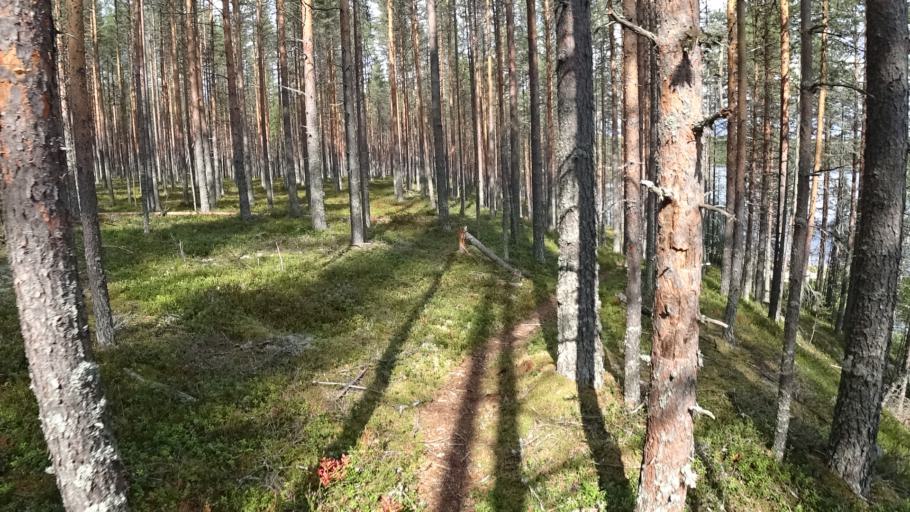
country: FI
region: North Karelia
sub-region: Joensuu
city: Ilomantsi
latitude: 62.6066
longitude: 31.1891
